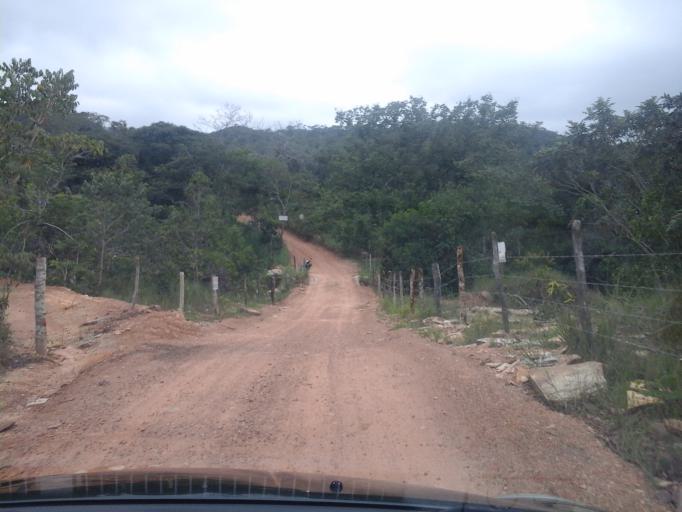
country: BR
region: Goias
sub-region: Pirenopolis
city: Pirenopolis
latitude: -15.7453
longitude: -49.0420
